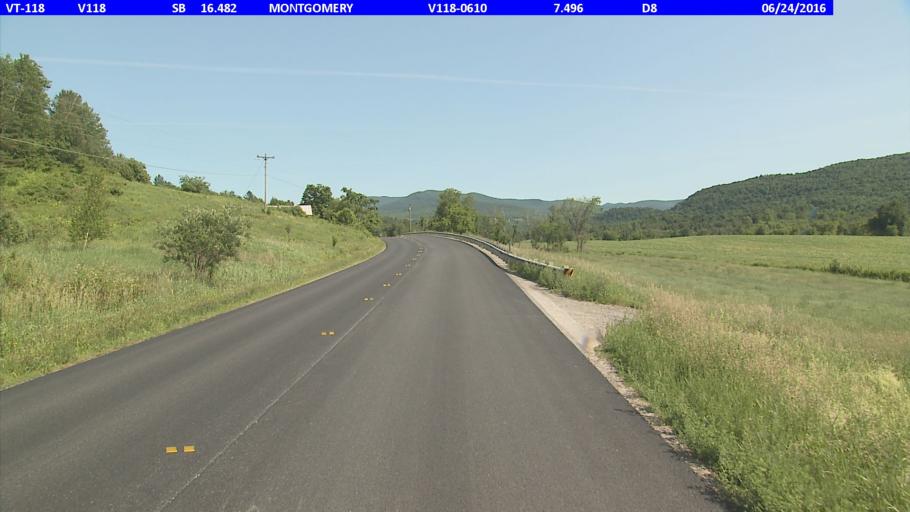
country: US
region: Vermont
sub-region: Franklin County
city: Richford
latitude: 44.8982
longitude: -72.6308
